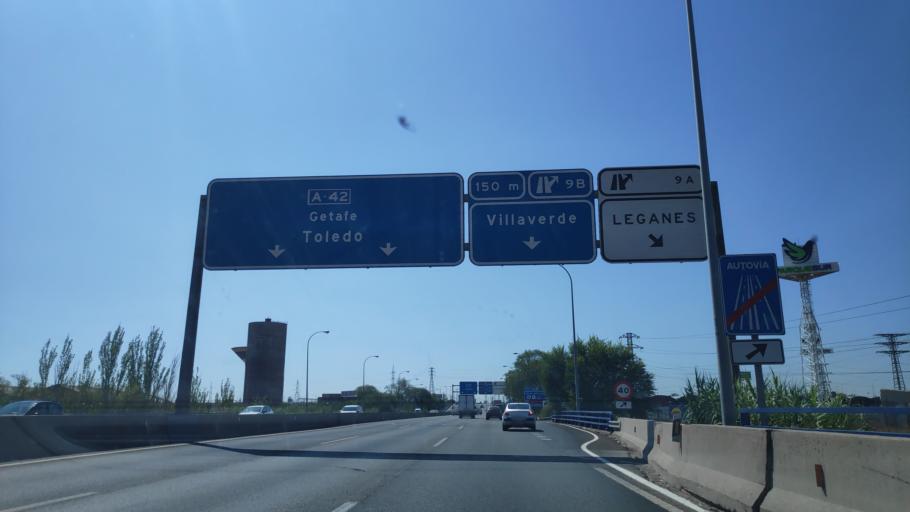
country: ES
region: Madrid
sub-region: Provincia de Madrid
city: Villaverde
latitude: 40.3420
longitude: -3.7240
